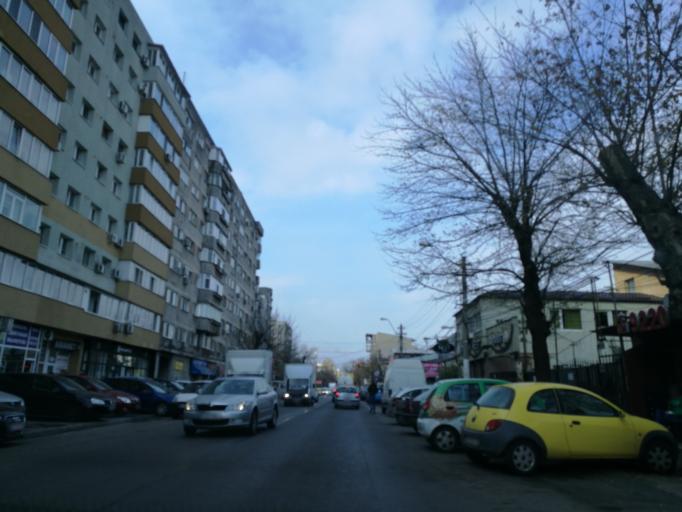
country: RO
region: Ilfov
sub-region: Comuna Chiajna
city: Rosu
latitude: 44.4401
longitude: 26.0267
